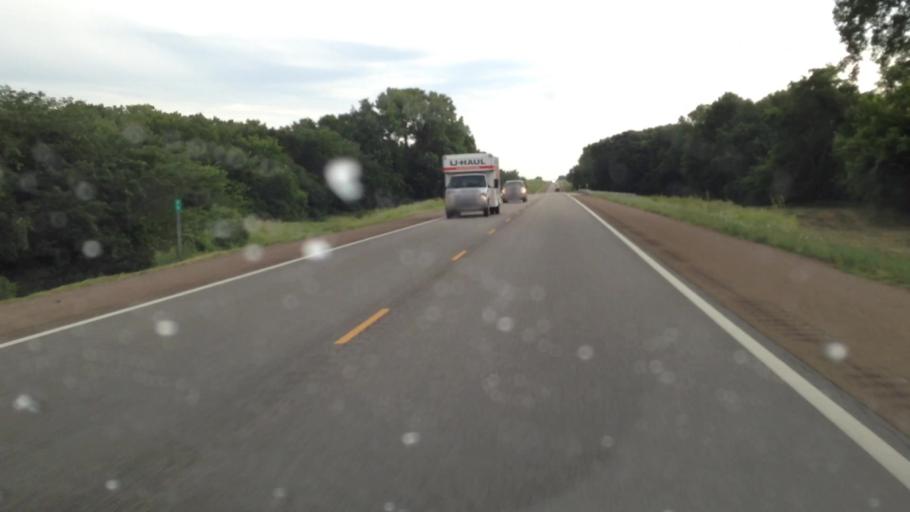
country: US
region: Kansas
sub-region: Woodson County
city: Yates Center
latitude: 38.0287
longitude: -95.7391
